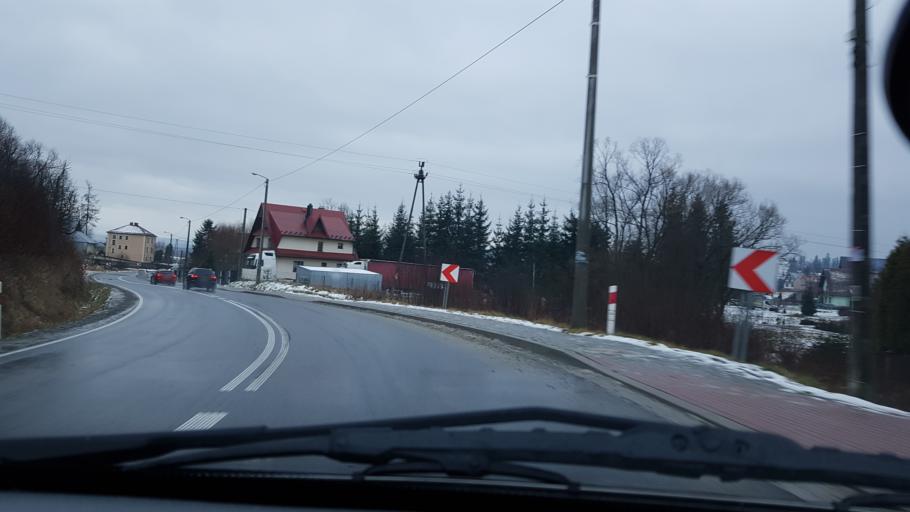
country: PL
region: Lesser Poland Voivodeship
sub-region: Powiat nowotarski
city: Sieniawa
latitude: 49.5003
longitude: 19.8823
